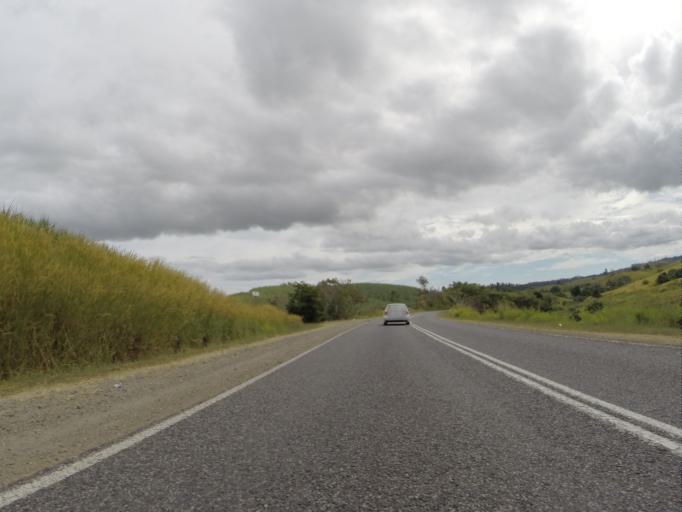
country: FJ
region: Western
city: Nadi
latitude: -18.0301
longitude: 177.3317
